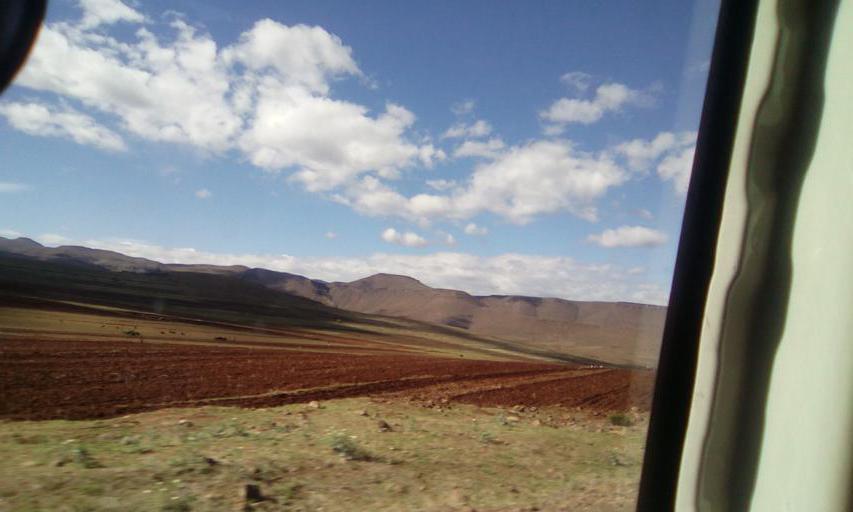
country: LS
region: Qacha's Nek
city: Qacha's Nek
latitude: -30.0227
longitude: 28.1937
